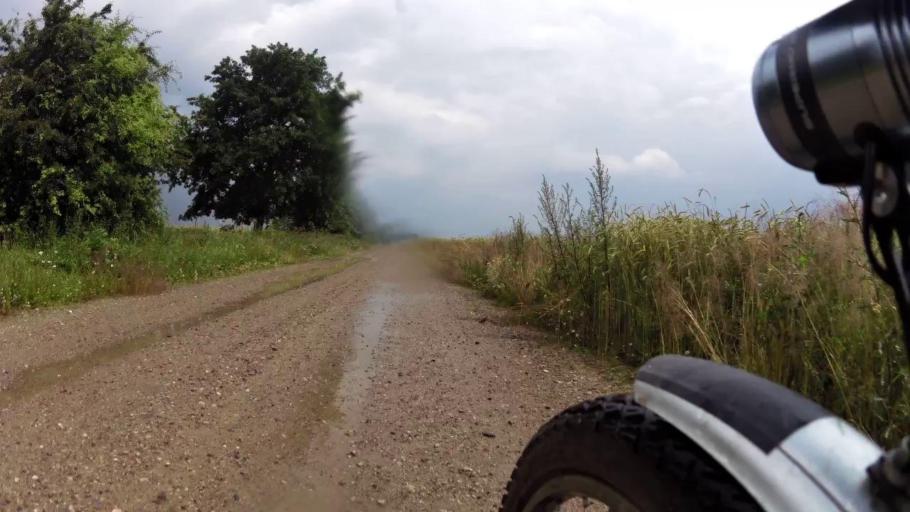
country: PL
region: West Pomeranian Voivodeship
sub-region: Powiat lobeski
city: Lobez
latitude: 53.7067
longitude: 15.6171
